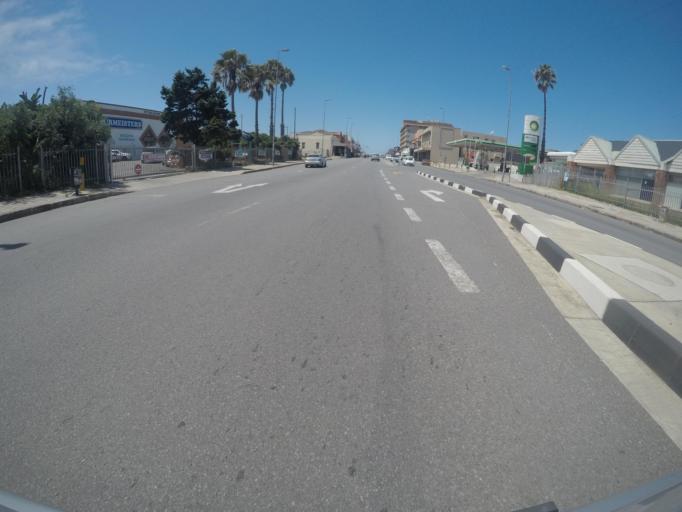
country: ZA
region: Eastern Cape
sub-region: Buffalo City Metropolitan Municipality
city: East London
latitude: -33.0182
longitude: 27.9108
